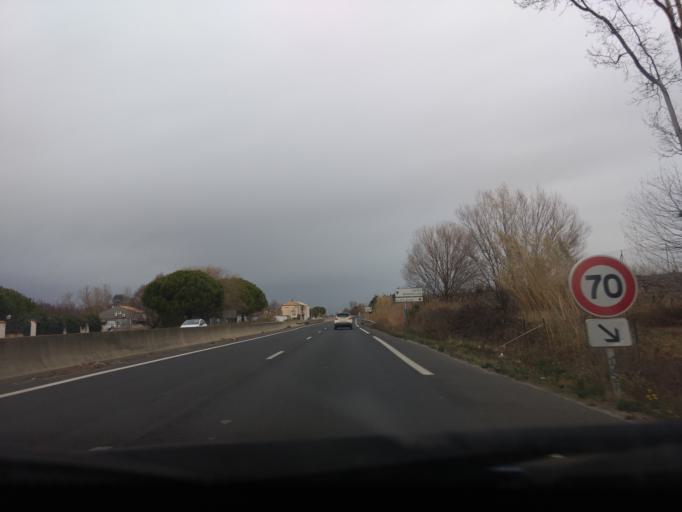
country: FR
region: Languedoc-Roussillon
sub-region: Departement de l'Herault
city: Lattes
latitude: 43.5581
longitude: 3.8931
